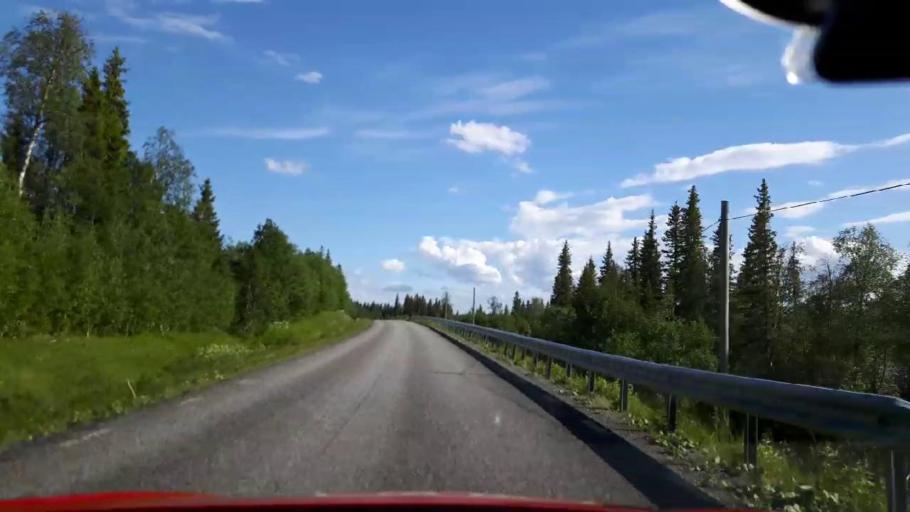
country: SE
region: Jaemtland
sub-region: Krokoms Kommun
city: Valla
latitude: 63.7077
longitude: 14.1425
